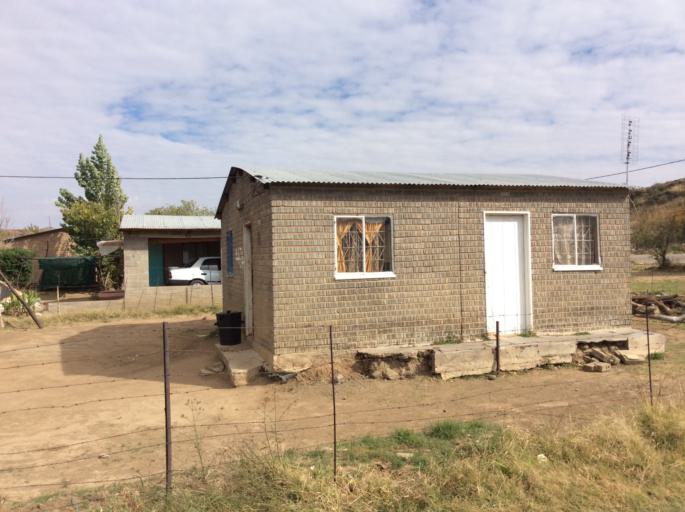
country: LS
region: Mafeteng
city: Mafeteng
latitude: -29.7174
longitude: 27.0177
